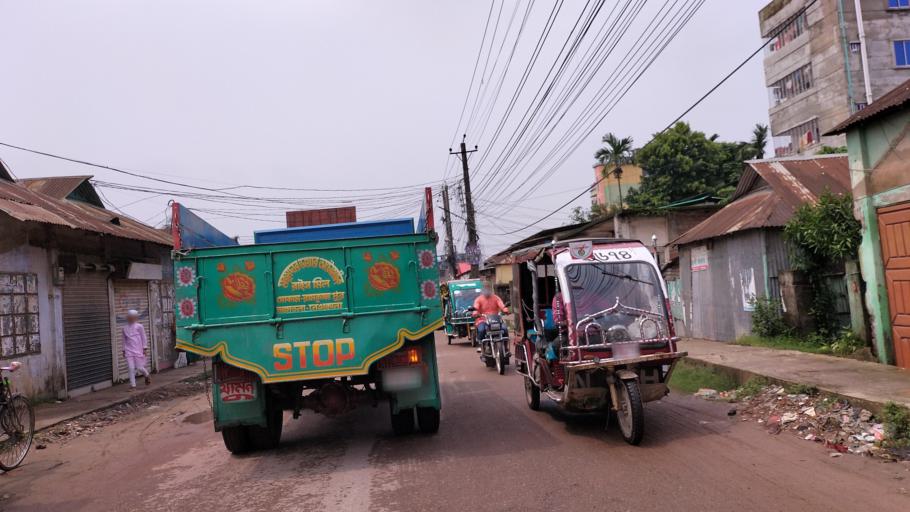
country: BD
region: Dhaka
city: Netrakona
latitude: 24.8890
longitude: 90.7384
